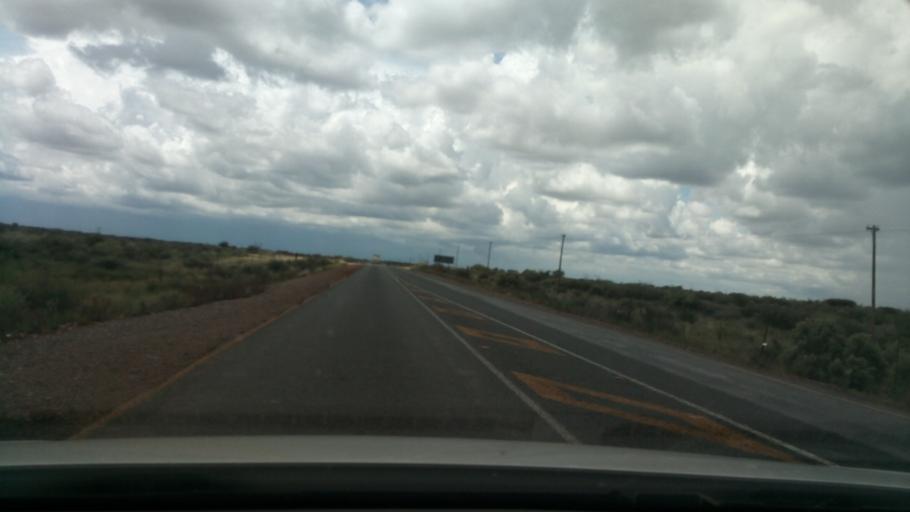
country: ZA
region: Northern Cape
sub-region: Siyanda District Municipality
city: Danielskuil
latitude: -28.2621
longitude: 23.5615
